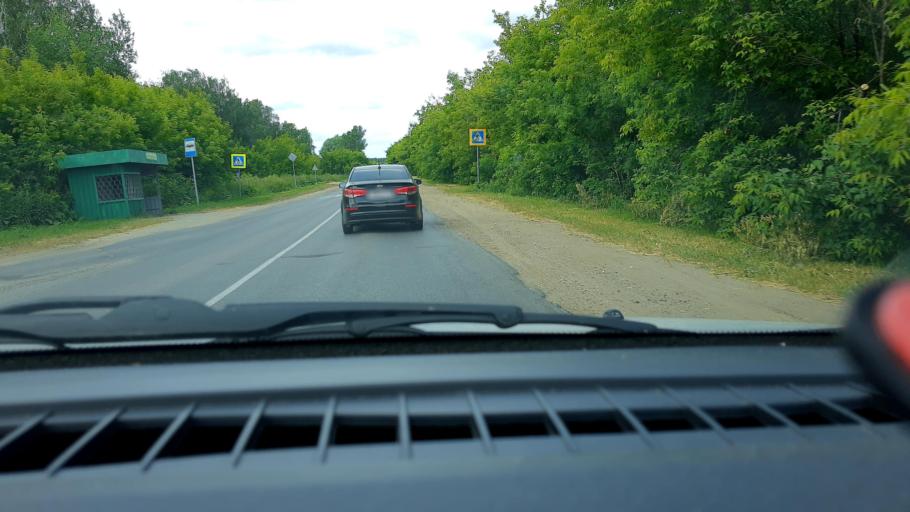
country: RU
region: Nizjnij Novgorod
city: Kstovo
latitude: 56.1334
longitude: 44.0975
